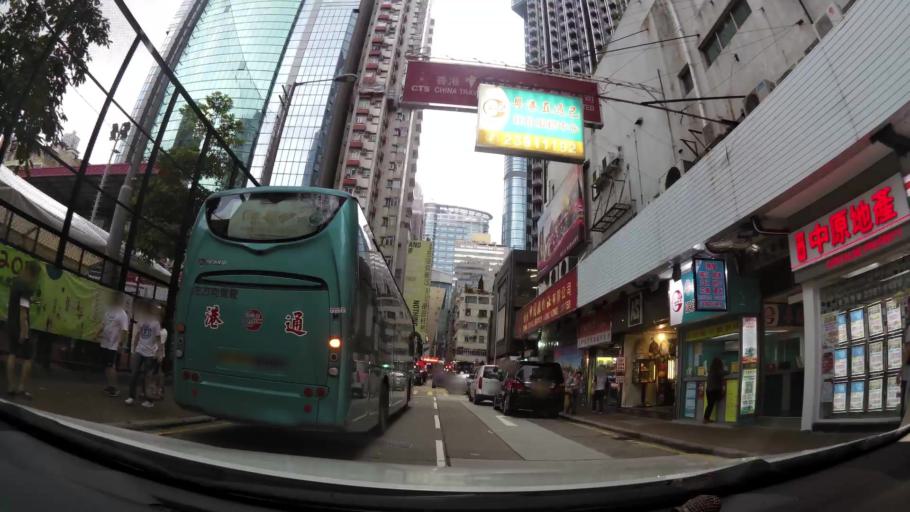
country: HK
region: Kowloon City
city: Kowloon
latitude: 22.3189
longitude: 114.1724
